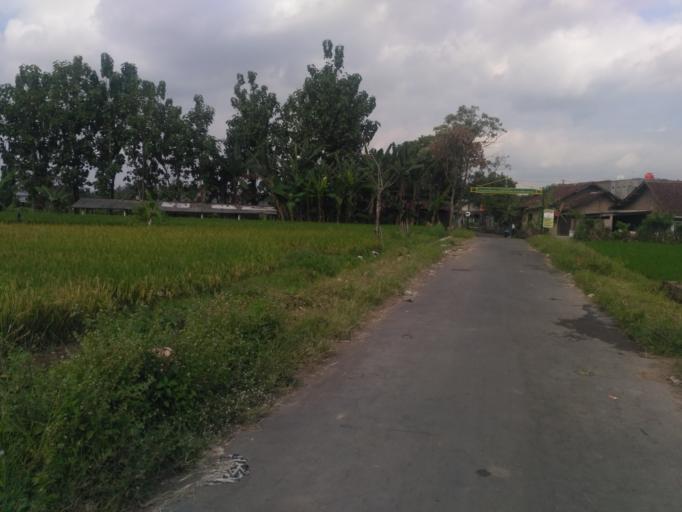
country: ID
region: Daerah Istimewa Yogyakarta
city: Yogyakarta
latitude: -7.7608
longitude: 110.3537
